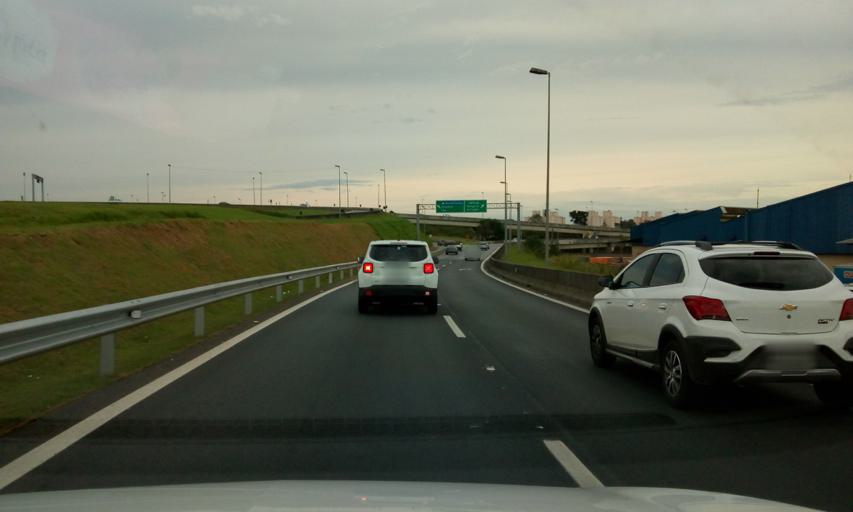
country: BR
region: Sao Paulo
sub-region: Jundiai
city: Jundiai
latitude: -23.1730
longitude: -46.9212
